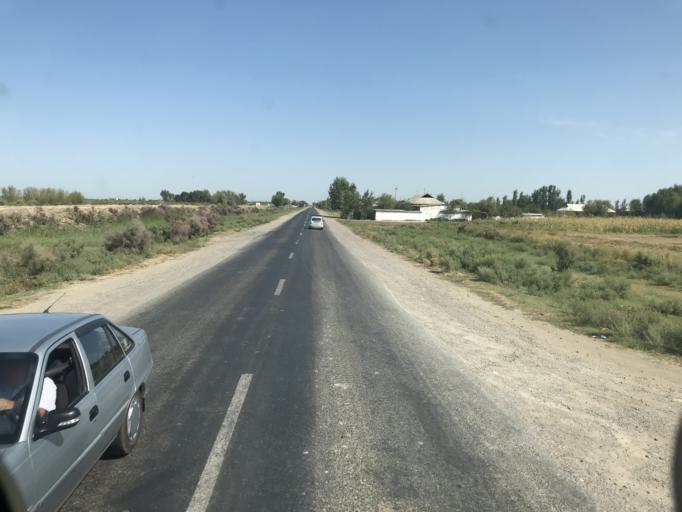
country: KZ
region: Ongtustik Qazaqstan
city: Myrzakent
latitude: 40.7542
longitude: 68.5370
